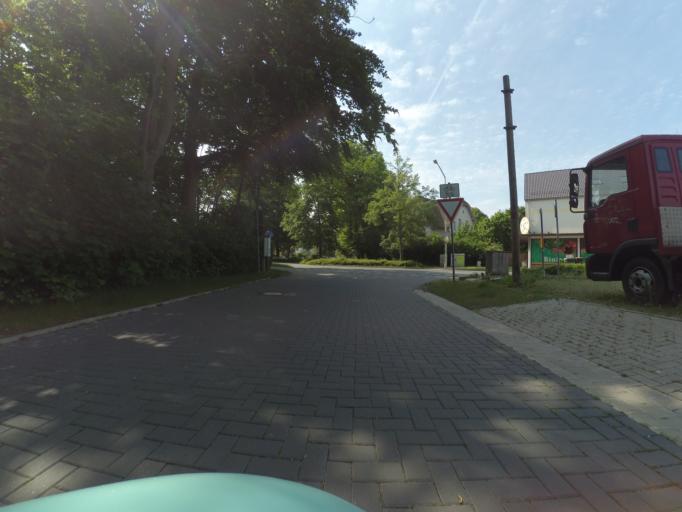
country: DE
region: Lower Saxony
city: Sehnde
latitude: 52.3177
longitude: 9.9600
